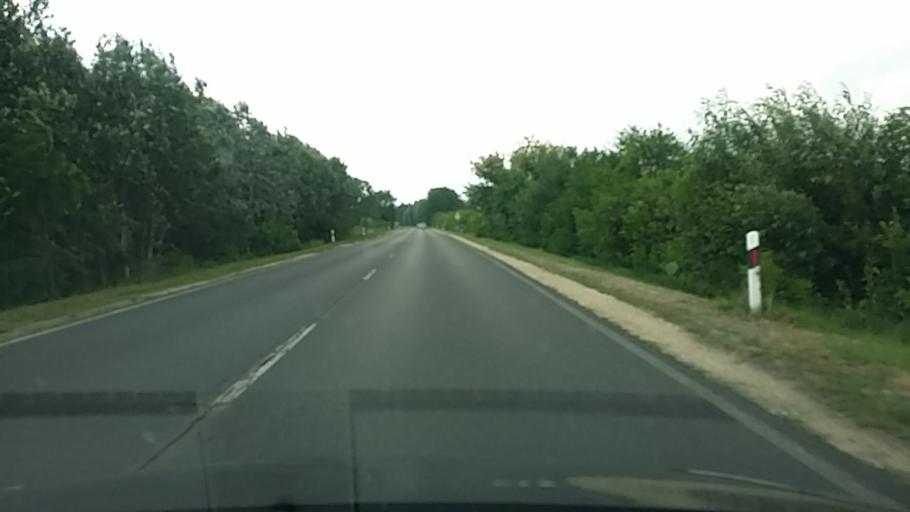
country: HU
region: Pest
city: Taborfalva
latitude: 47.1051
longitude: 19.4636
